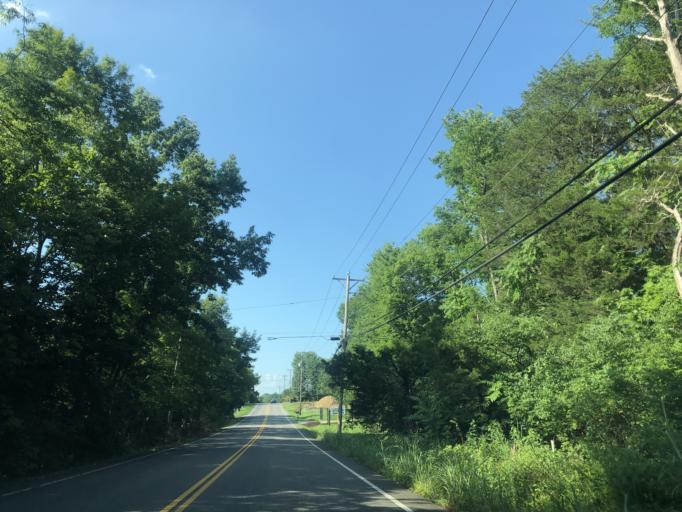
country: US
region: Tennessee
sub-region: Wilson County
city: Green Hill
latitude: 36.1478
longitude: -86.5845
